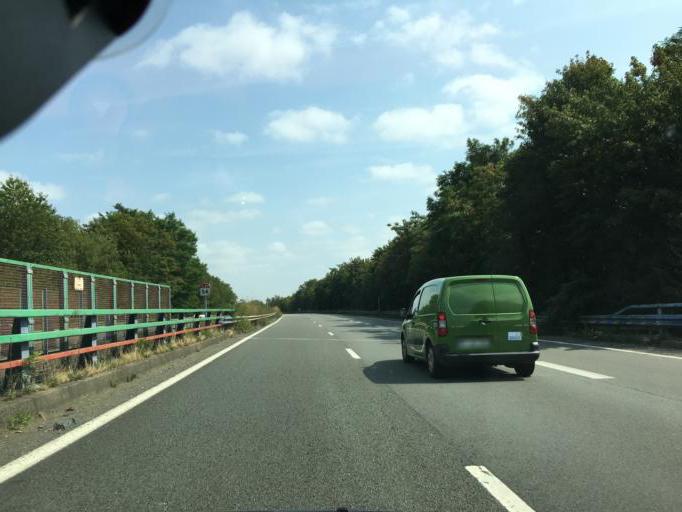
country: FR
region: Nord-Pas-de-Calais
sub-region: Departement du Nord
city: Escaudain
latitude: 50.3236
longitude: 3.3477
